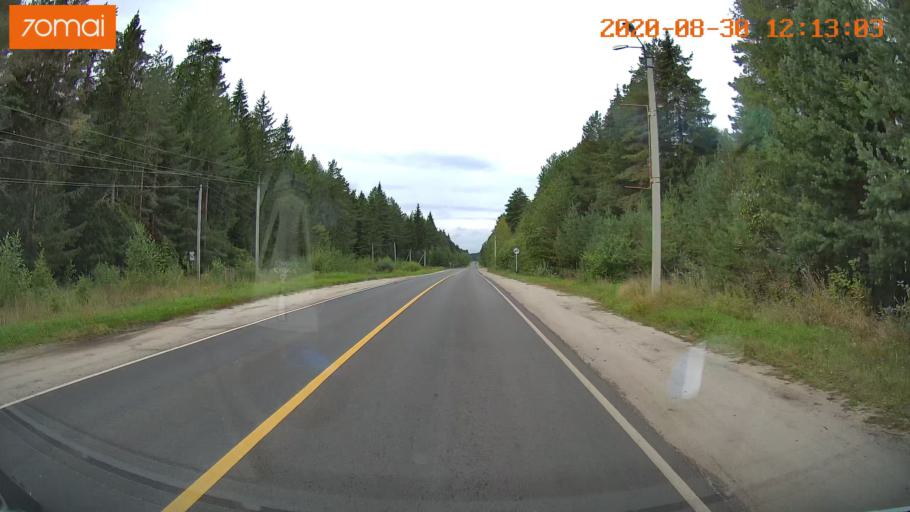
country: RU
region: Ivanovo
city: Yur'yevets
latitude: 57.3121
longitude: 43.0862
